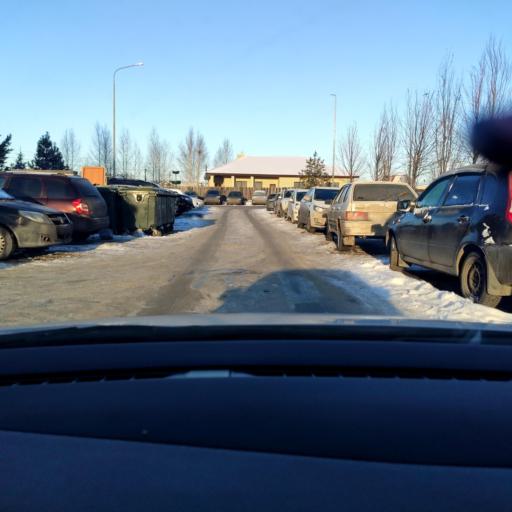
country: RU
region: Tatarstan
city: Stolbishchi
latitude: 55.6900
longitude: 49.2009
